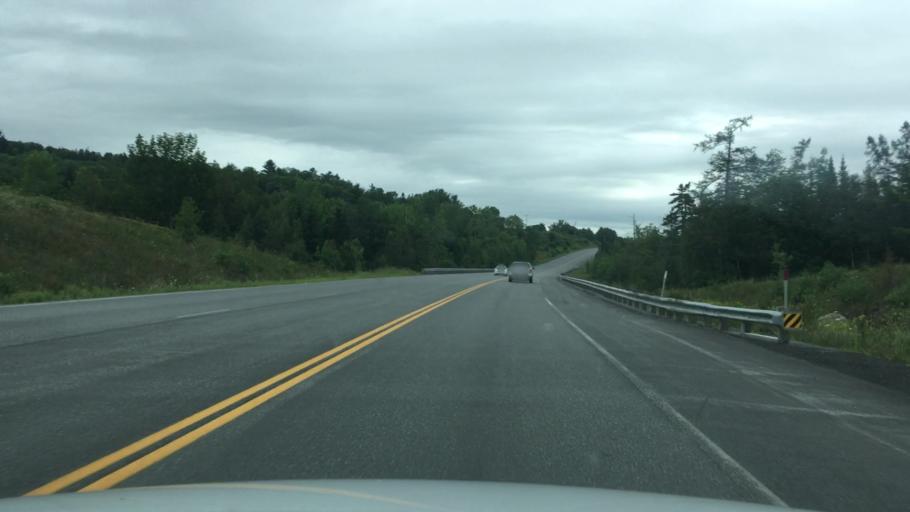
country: US
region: Maine
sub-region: Hancock County
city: Franklin
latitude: 44.8558
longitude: -68.3233
